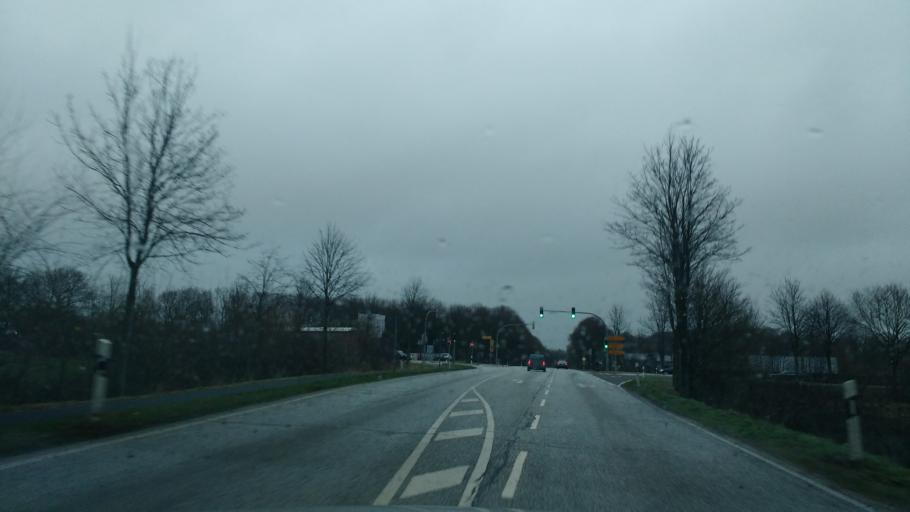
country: DE
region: Schleswig-Holstein
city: Hohenwestedt
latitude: 54.0833
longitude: 9.6613
